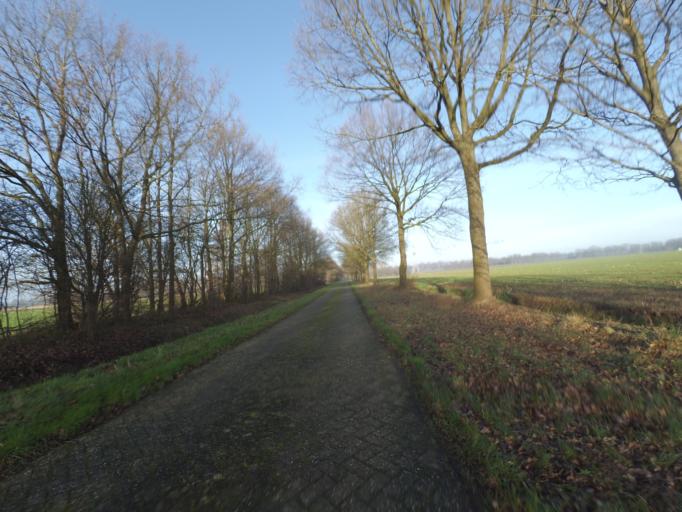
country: NL
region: Drenthe
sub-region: Gemeente Coevorden
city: Sleen
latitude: 52.8387
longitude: 6.7073
